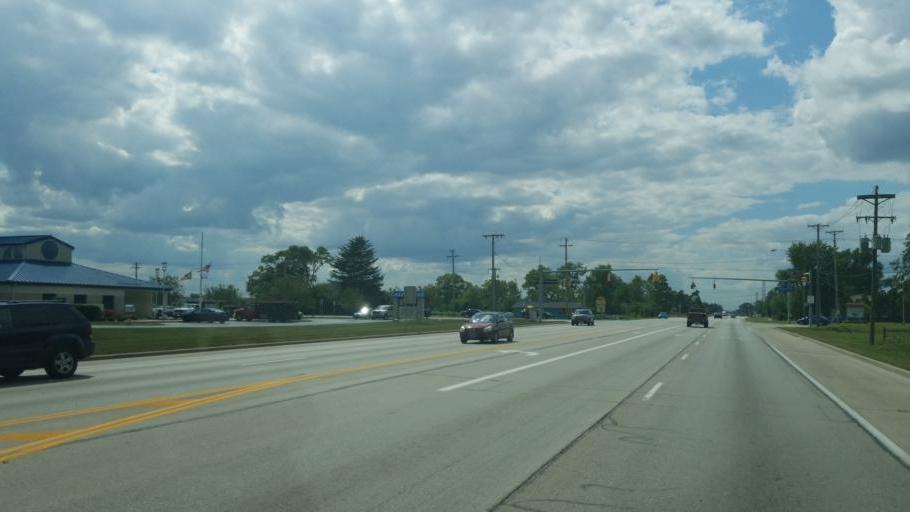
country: US
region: Ohio
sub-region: Wood County
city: Northwood
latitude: 41.6375
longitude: -83.4464
